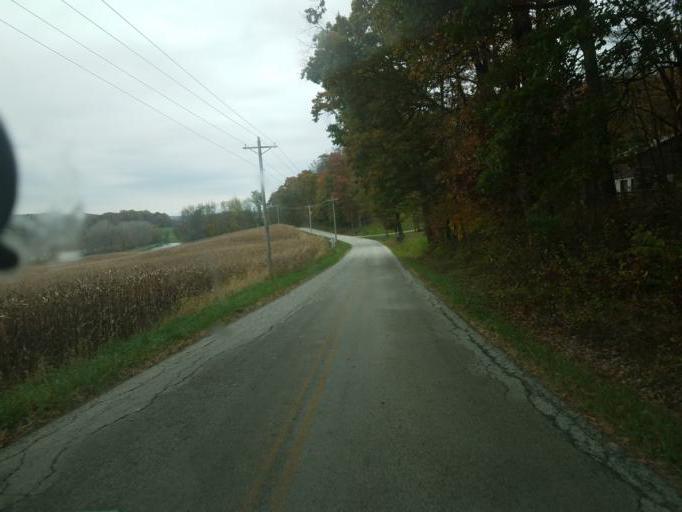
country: US
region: Ohio
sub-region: Ashland County
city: Loudonville
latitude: 40.6236
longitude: -82.1662
